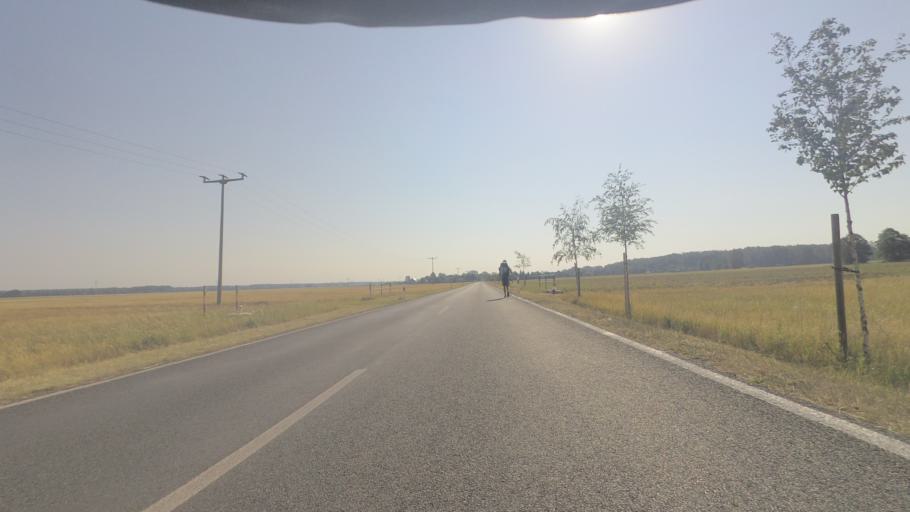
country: DE
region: Saxony-Anhalt
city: Quellendorf
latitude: 51.8145
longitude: 12.1049
